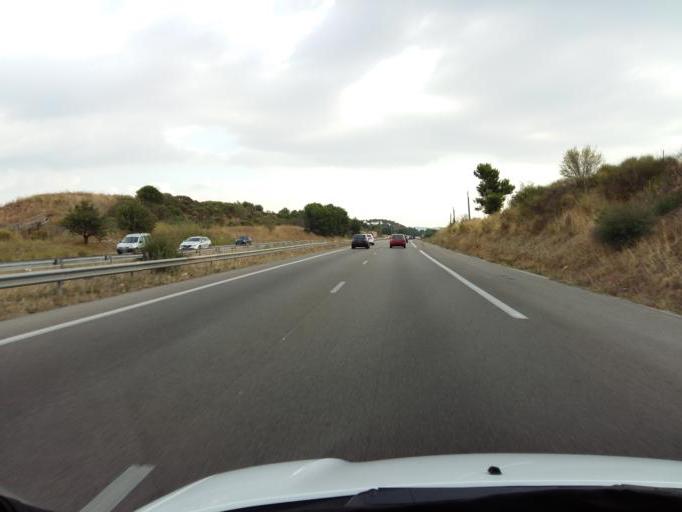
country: FR
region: Provence-Alpes-Cote d'Azur
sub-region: Departement des Bouches-du-Rhone
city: Bouc-Bel-Air
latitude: 43.4824
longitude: 5.4081
